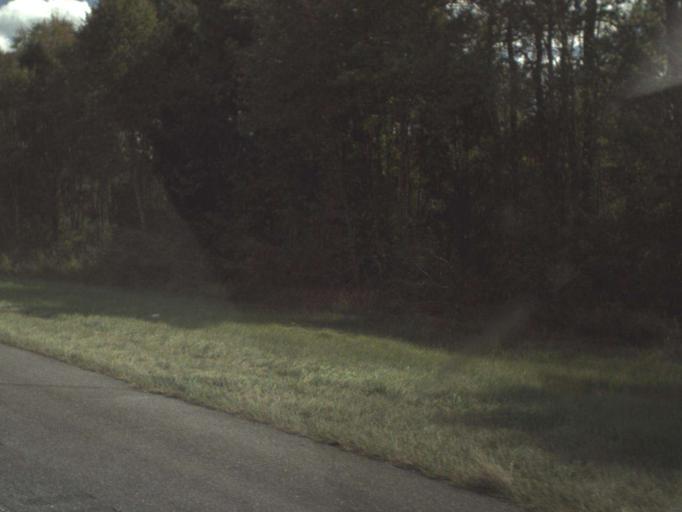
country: US
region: Florida
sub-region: Jackson County
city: Marianna
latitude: 30.7151
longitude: -85.1616
